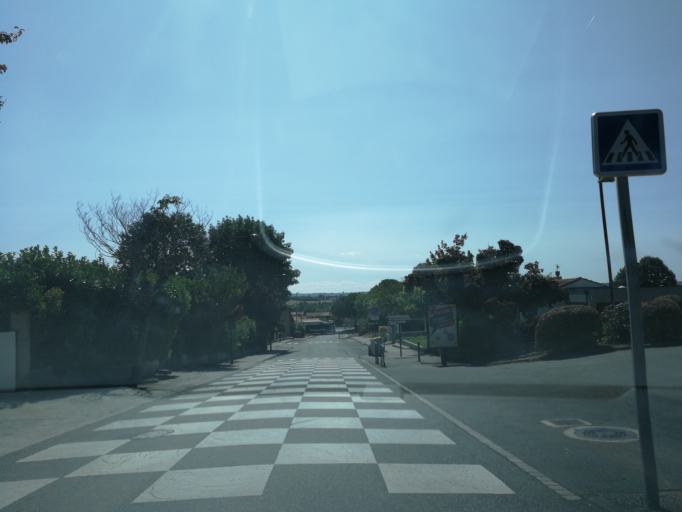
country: FR
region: Midi-Pyrenees
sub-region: Departement de la Haute-Garonne
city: Flourens
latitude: 43.5854
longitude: 1.5329
